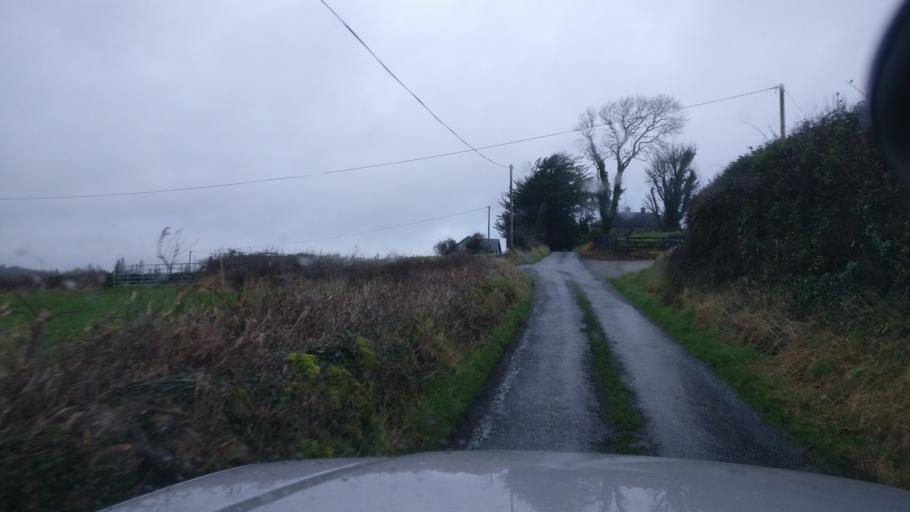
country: IE
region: Connaught
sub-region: County Galway
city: Loughrea
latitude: 53.1630
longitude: -8.6104
